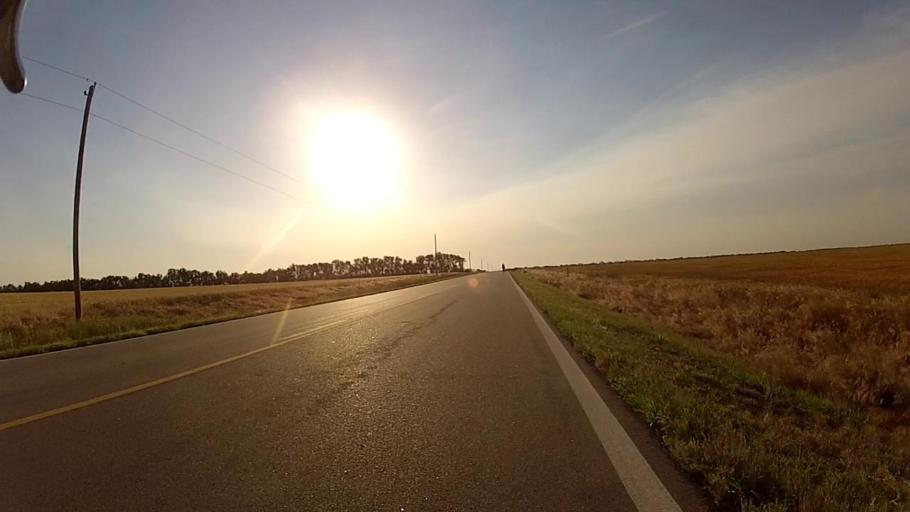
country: US
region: Kansas
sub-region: Sumner County
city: Caldwell
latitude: 37.1544
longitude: -97.7953
